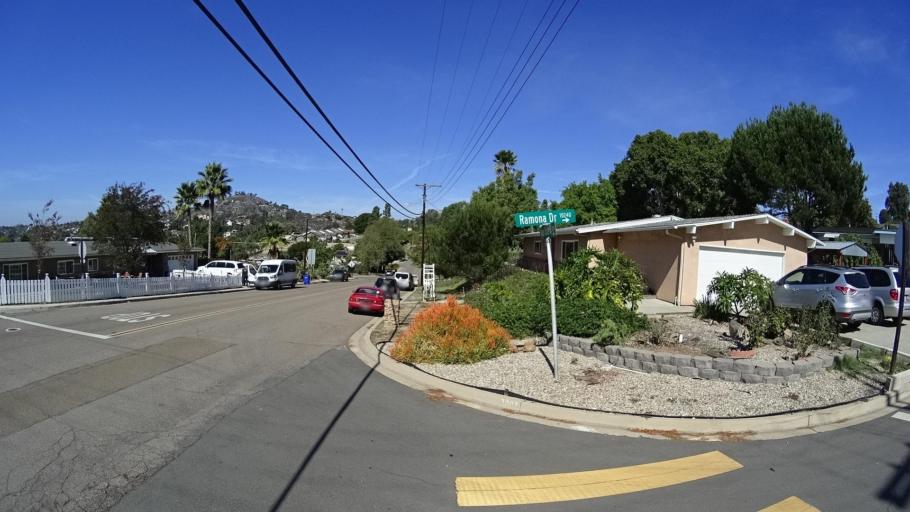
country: US
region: California
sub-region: San Diego County
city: Casa de Oro-Mount Helix
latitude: 32.7478
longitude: -116.9722
